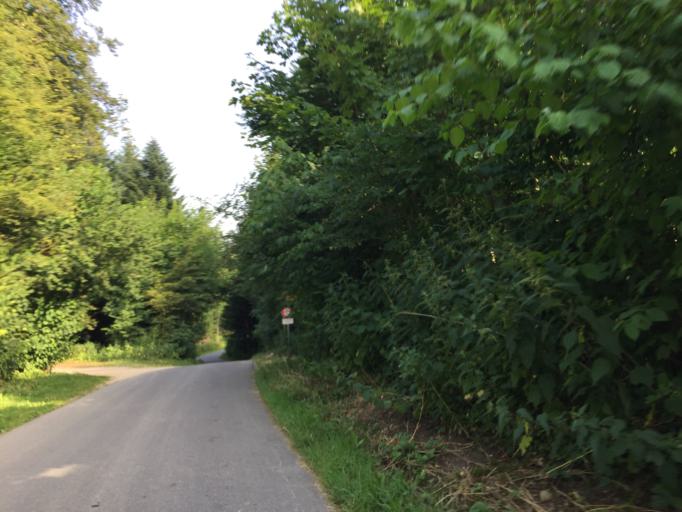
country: CH
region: Bern
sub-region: Bern-Mittelland District
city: Muri
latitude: 46.9273
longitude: 7.5156
